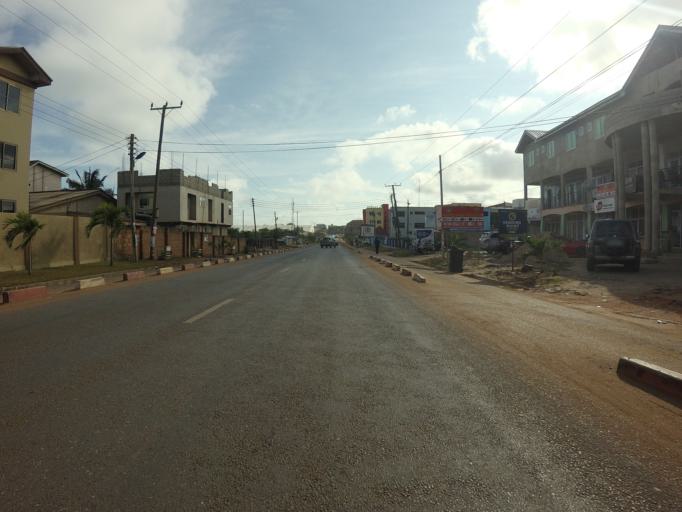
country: GH
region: Greater Accra
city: Teshi Old Town
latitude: 5.5737
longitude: -0.1408
